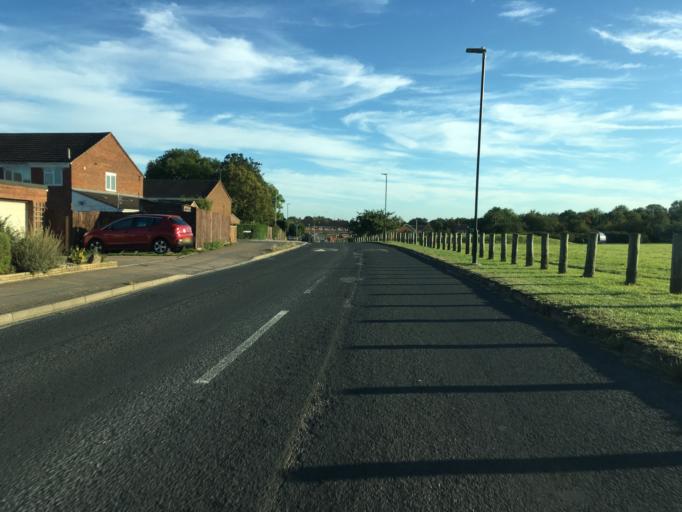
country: GB
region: England
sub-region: Worcestershire
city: Bredon
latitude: 52.0057
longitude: -2.1199
